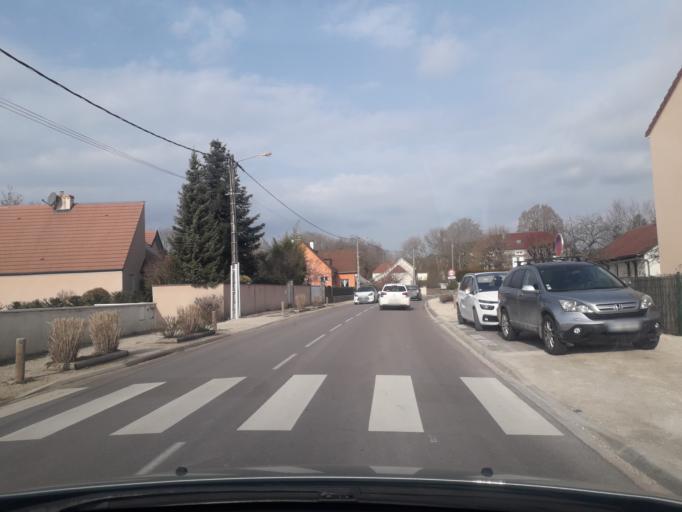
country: FR
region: Bourgogne
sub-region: Departement de la Cote-d'Or
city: Messigny-et-Vantoux
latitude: 47.4016
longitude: 5.0199
